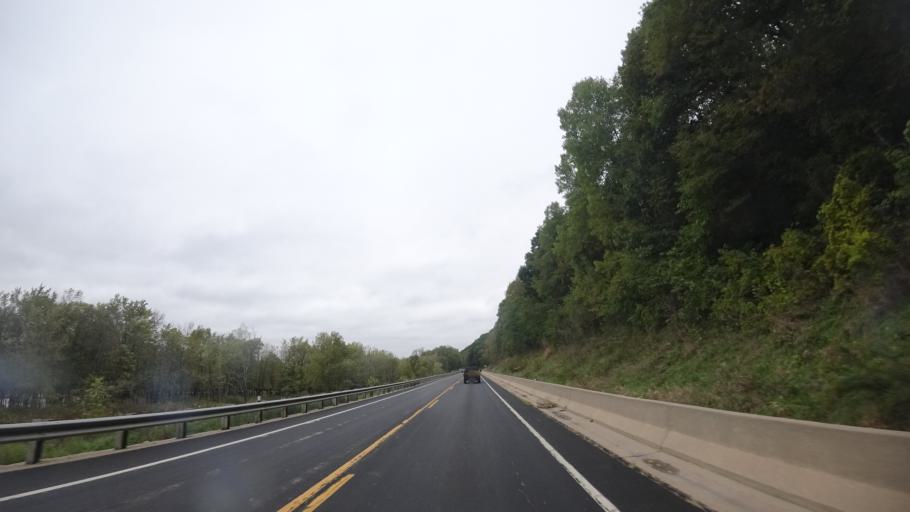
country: US
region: Wisconsin
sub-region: Grant County
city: Boscobel
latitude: 43.1307
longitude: -90.7559
